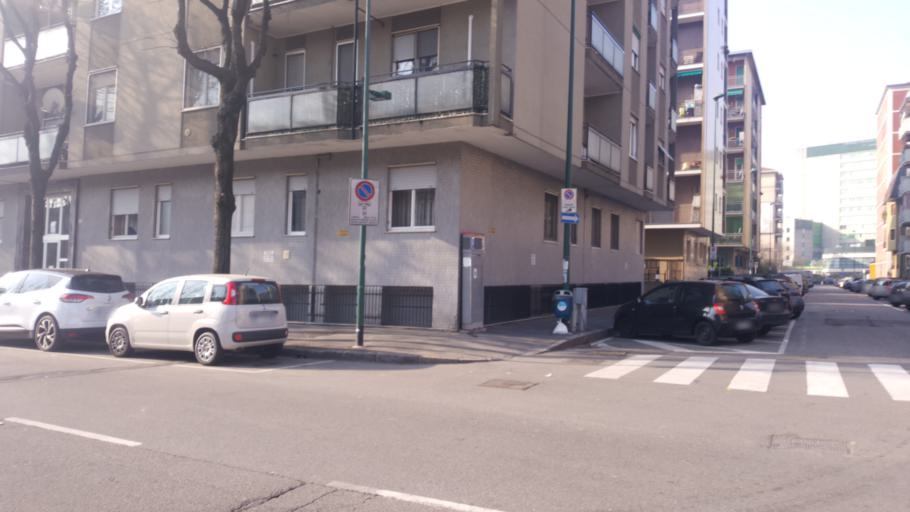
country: IT
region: Lombardy
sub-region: Citta metropolitana di Milano
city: Sesto San Giovanni
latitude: 45.5367
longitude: 9.2229
